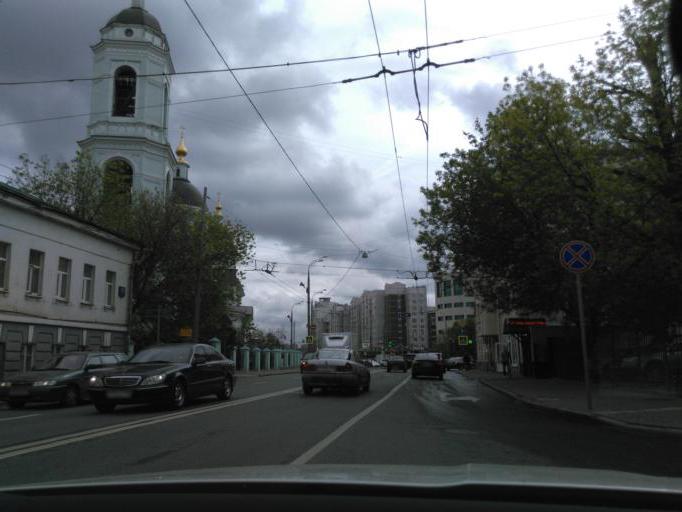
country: RU
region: Moscow
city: Taganskiy
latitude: 55.7465
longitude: 37.6667
